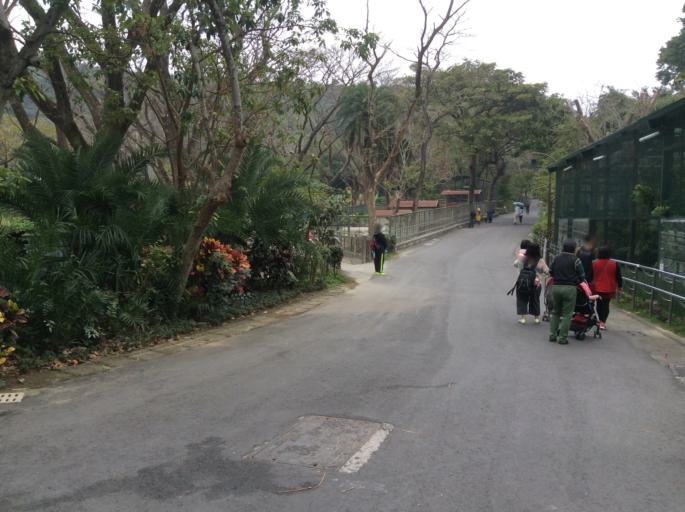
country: TW
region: Kaohsiung
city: Kaohsiung
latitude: 22.6356
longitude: 120.2761
